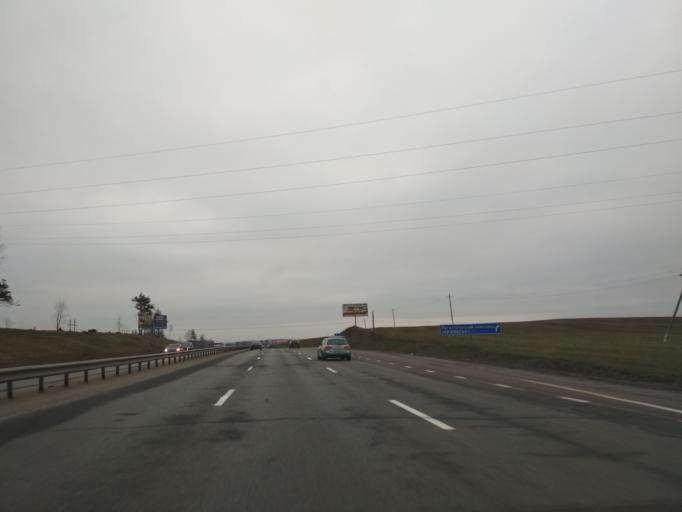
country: BY
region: Minsk
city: Pryvol'ny
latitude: 53.8152
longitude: 27.7723
